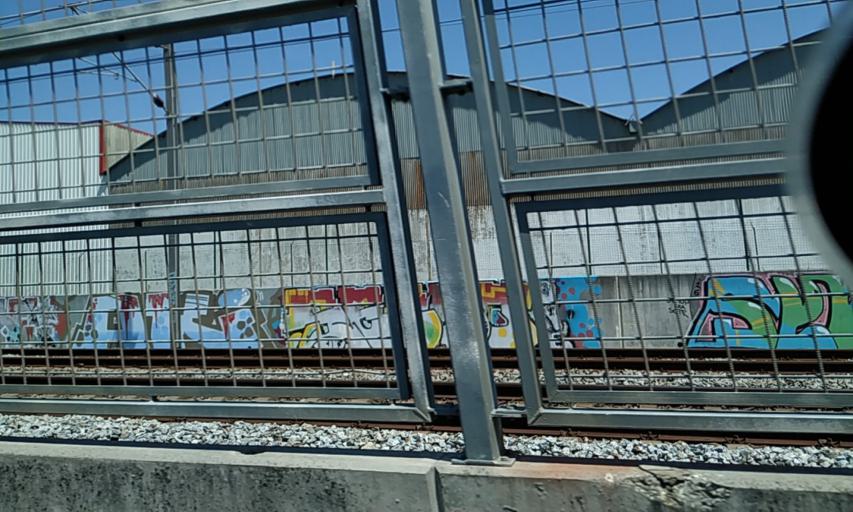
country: PT
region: Setubal
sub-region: Palmela
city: Palmela
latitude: 38.5732
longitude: -8.8732
